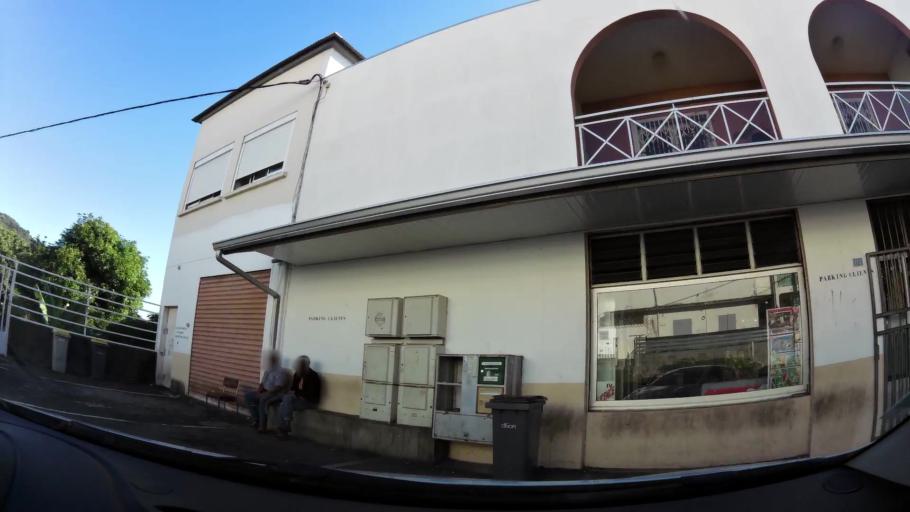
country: RE
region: Reunion
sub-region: Reunion
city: Saint-Denis
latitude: -20.8927
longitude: 55.4483
